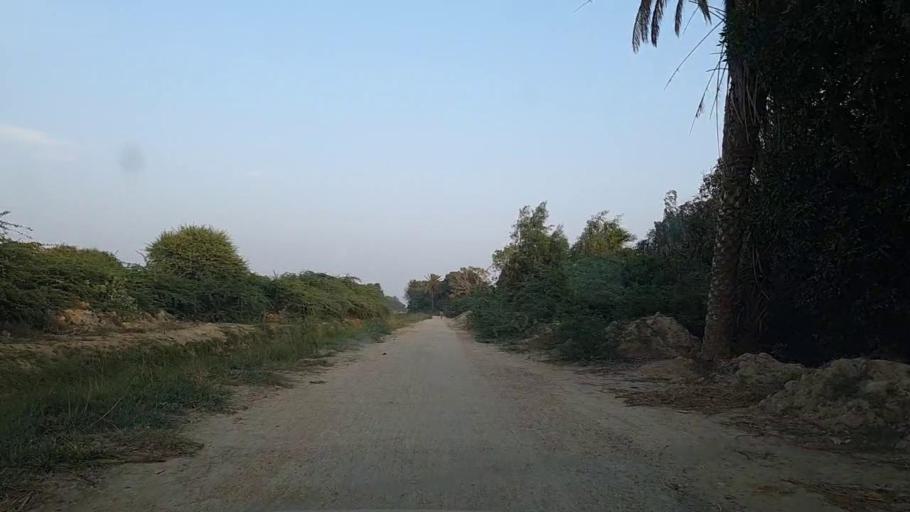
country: PK
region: Sindh
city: Mirpur Sakro
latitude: 24.6109
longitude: 67.5988
